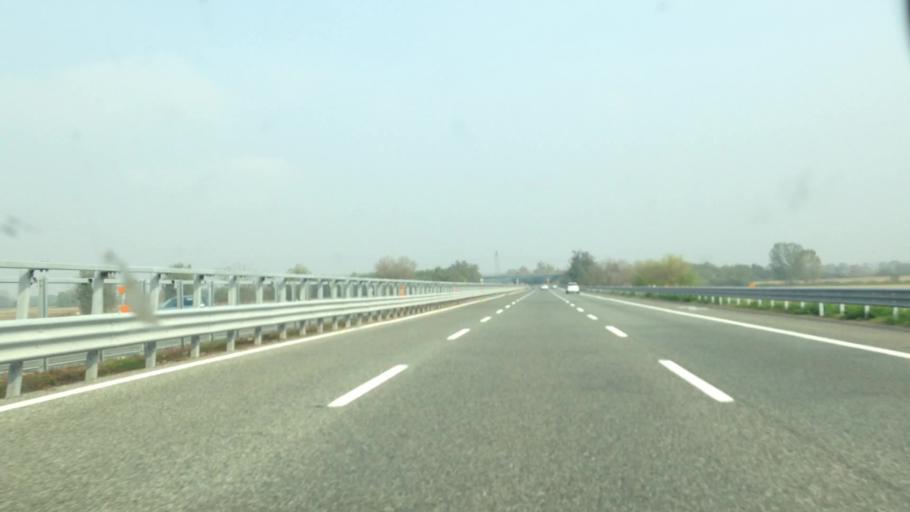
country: IT
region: Piedmont
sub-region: Provincia di Alessandria
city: Villanova Monferrato
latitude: 45.1755
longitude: 8.4942
